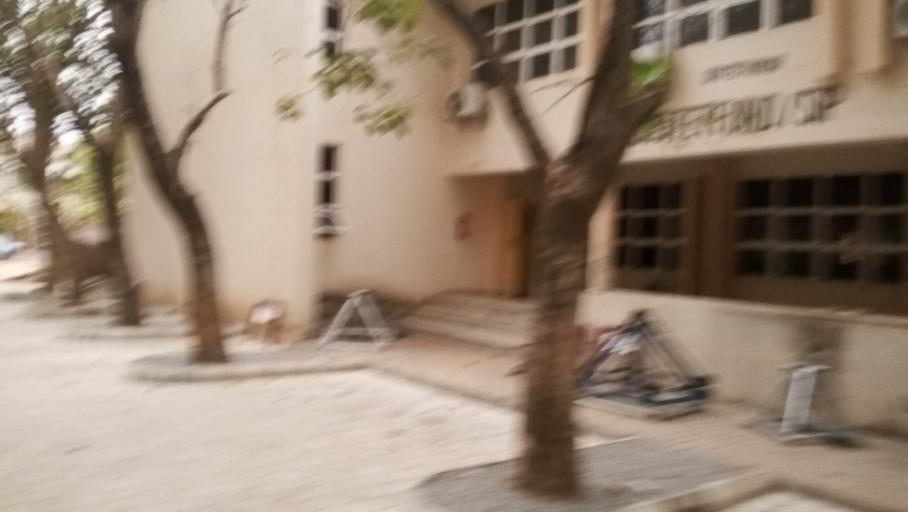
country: NG
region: Kaduna
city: Zaria
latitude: 11.1518
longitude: 7.6510
